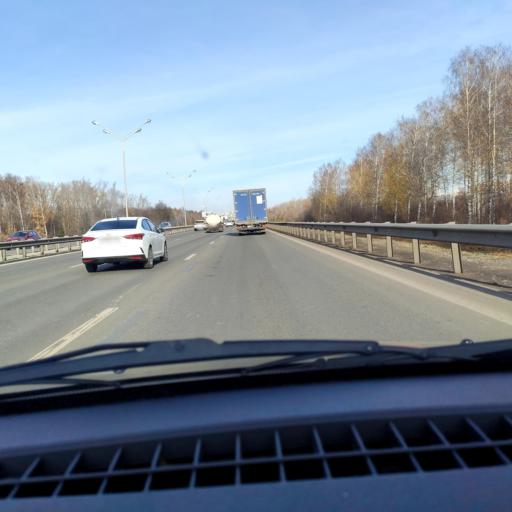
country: RU
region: Bashkortostan
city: Ufa
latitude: 54.6822
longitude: 55.9355
